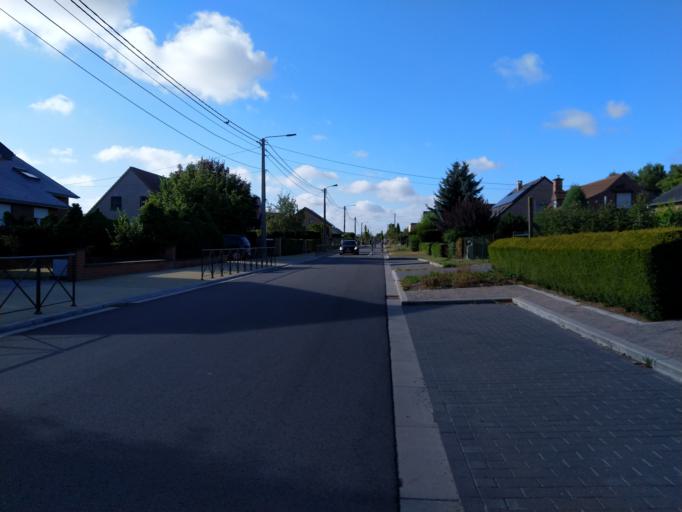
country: BE
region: Wallonia
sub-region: Province du Hainaut
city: Estinnes-au-Val
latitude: 50.4249
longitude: 4.1061
